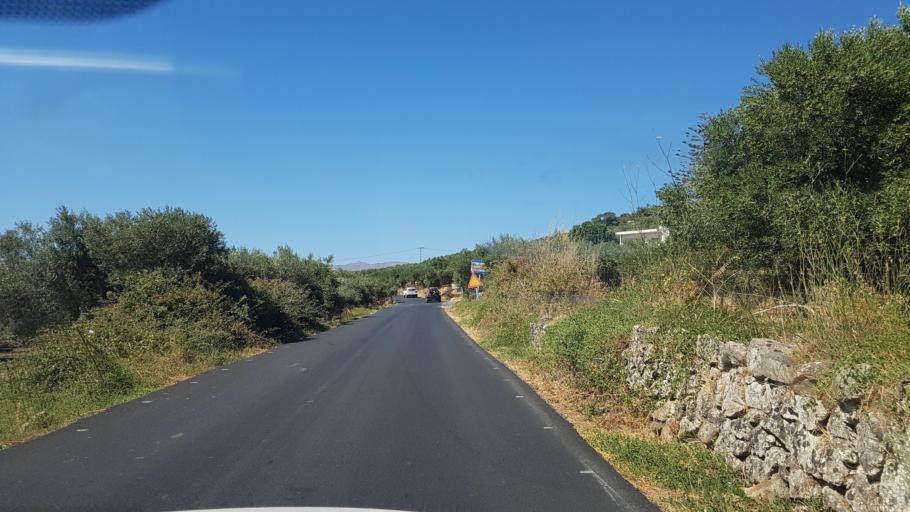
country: GR
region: Crete
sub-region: Nomos Chanias
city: Kissamos
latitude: 35.4879
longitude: 23.6910
